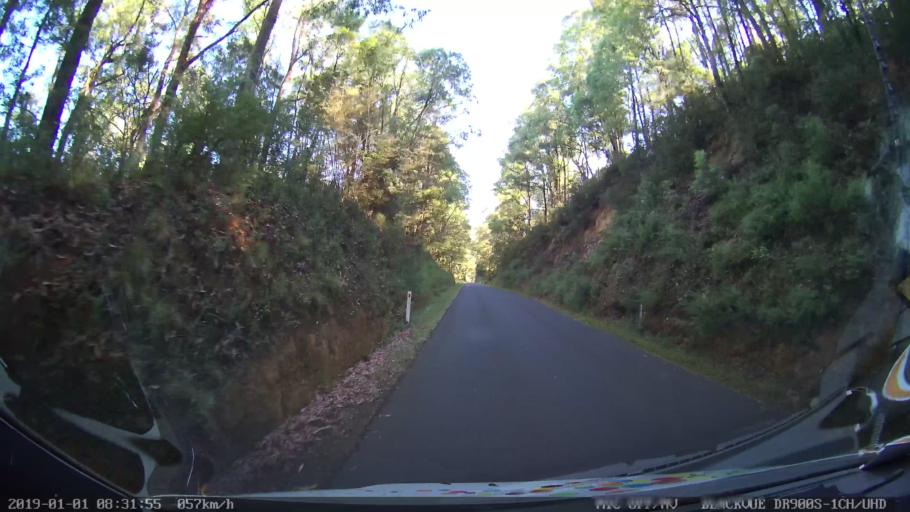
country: AU
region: New South Wales
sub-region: Snowy River
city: Jindabyne
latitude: -36.3663
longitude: 148.2056
